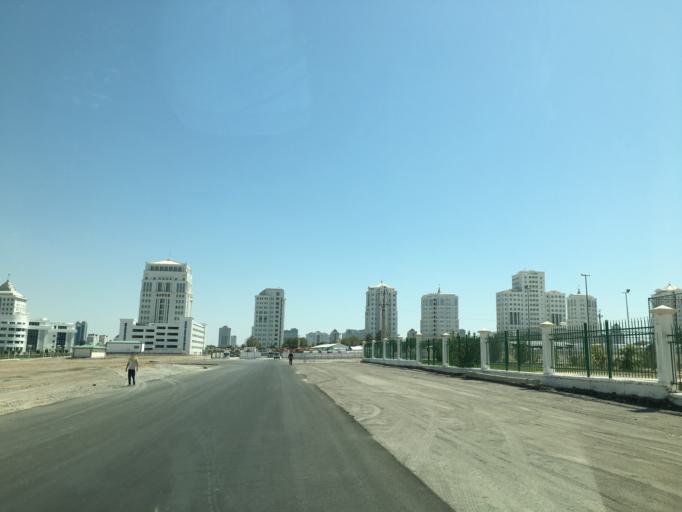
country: TM
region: Ahal
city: Ashgabat
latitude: 37.8910
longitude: 58.3708
